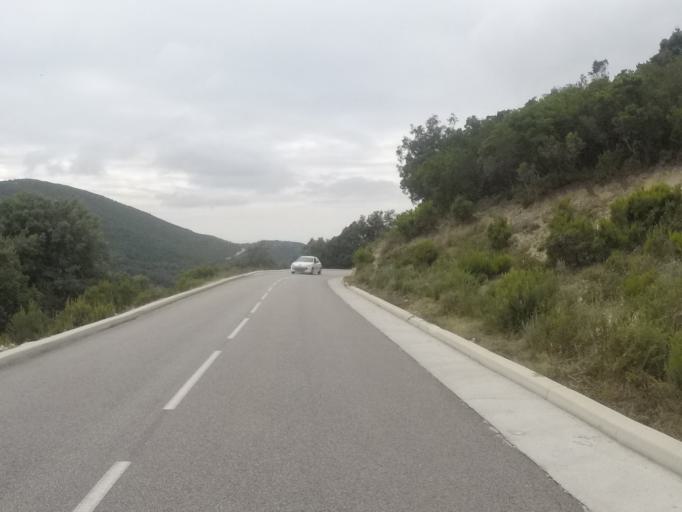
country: FR
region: Corsica
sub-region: Departement de la Corse-du-Sud
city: Pietrosella
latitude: 41.7921
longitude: 8.8233
